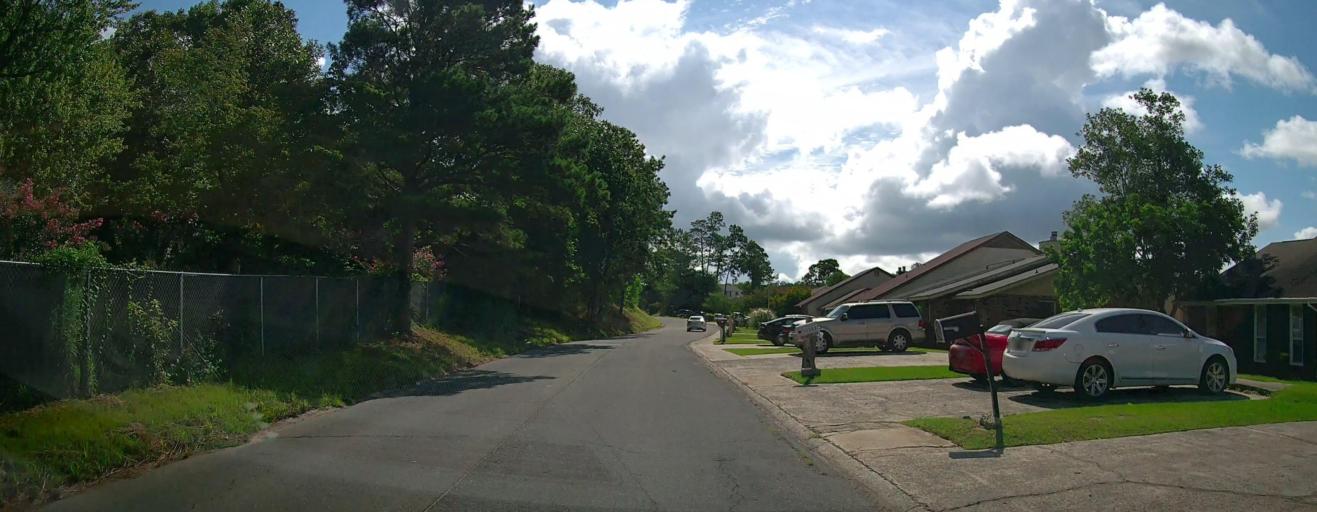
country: US
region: Georgia
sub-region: Houston County
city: Warner Robins
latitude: 32.5856
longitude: -83.6268
